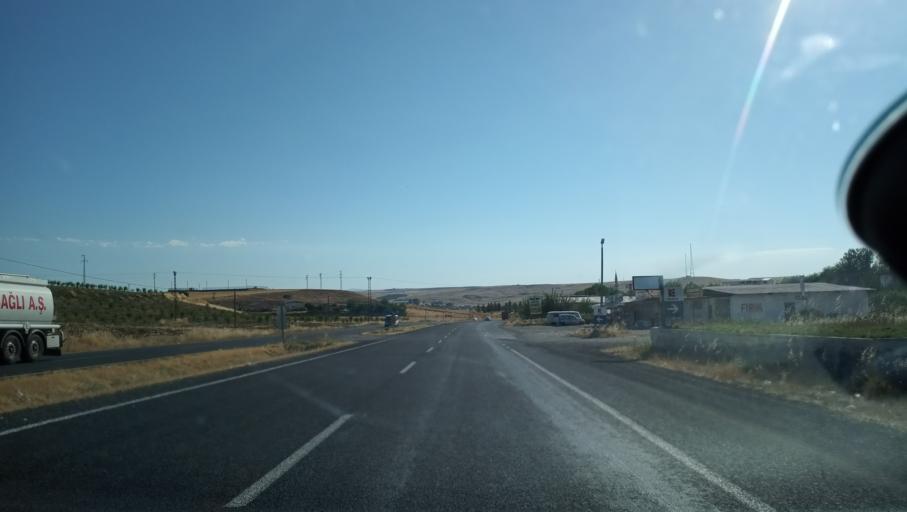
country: TR
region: Diyarbakir
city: Sur
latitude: 37.9885
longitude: 40.3725
